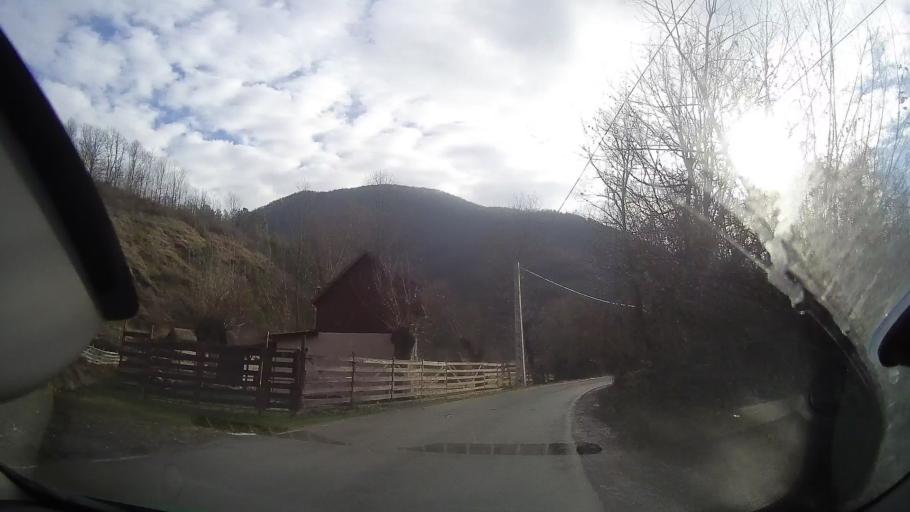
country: RO
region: Alba
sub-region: Comuna Ocolis
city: Ocolis
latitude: 46.4704
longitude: 23.4759
